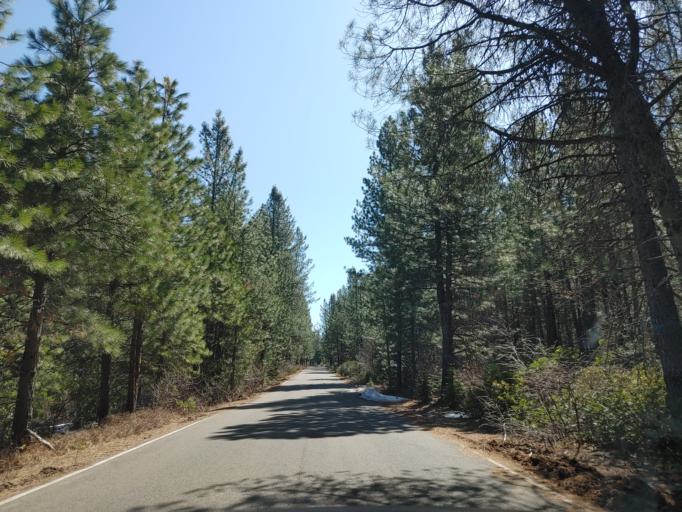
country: US
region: California
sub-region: Siskiyou County
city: McCloud
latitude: 41.2463
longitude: -122.0187
